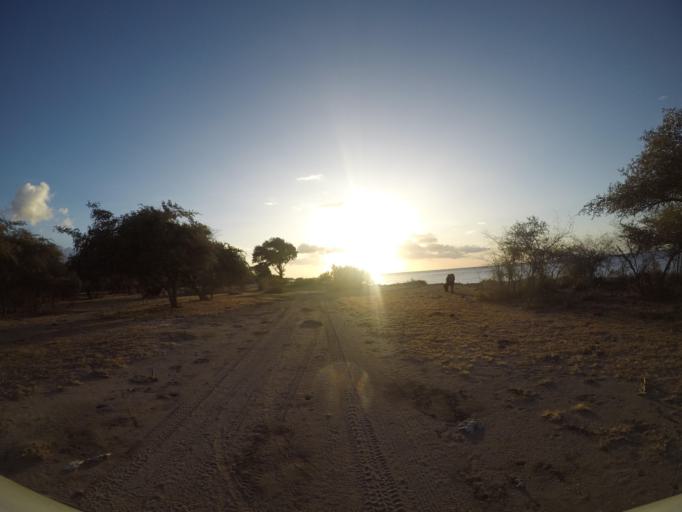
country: TL
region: Lautem
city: Lospalos
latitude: -8.3233
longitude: 126.9967
